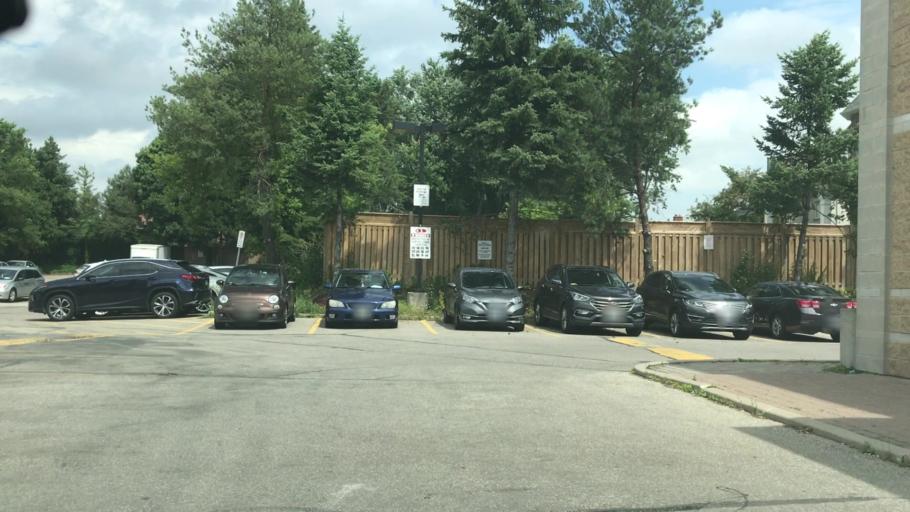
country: CA
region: Ontario
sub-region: York
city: Richmond Hill
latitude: 43.8417
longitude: -79.3971
